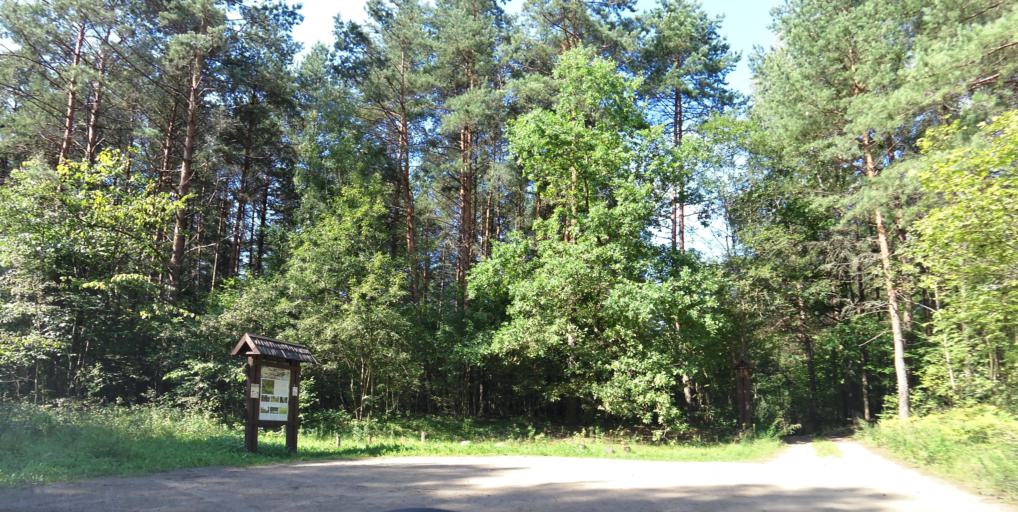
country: LT
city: Grigiskes
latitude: 54.7415
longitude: 25.0271
